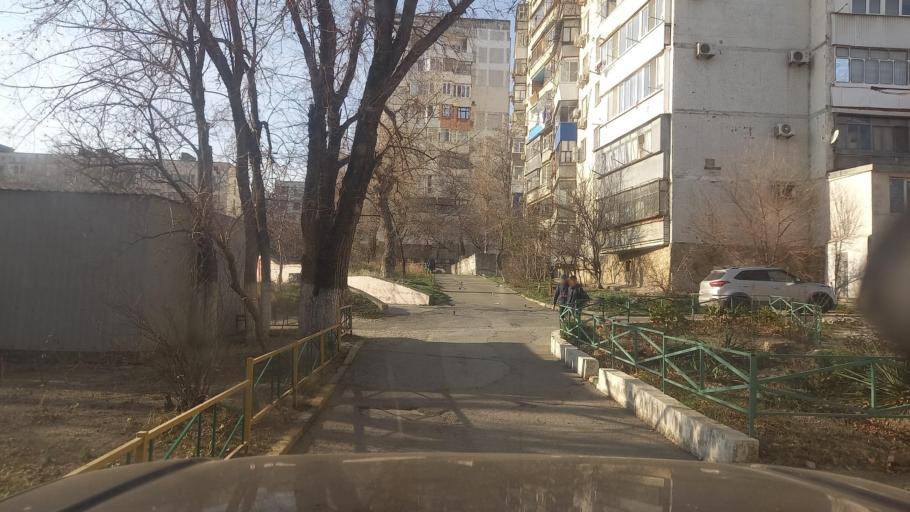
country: RU
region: Krasnodarskiy
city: Novorossiysk
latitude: 44.6887
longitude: 37.7763
